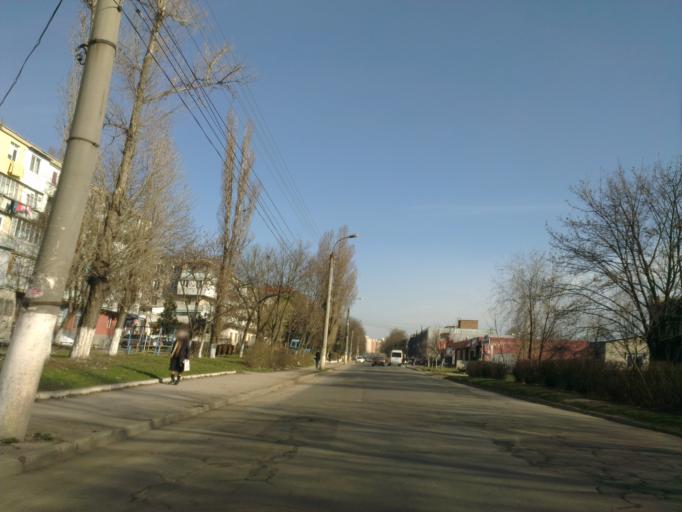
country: MD
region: Chisinau
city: Chisinau
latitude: 47.0225
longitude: 28.8832
